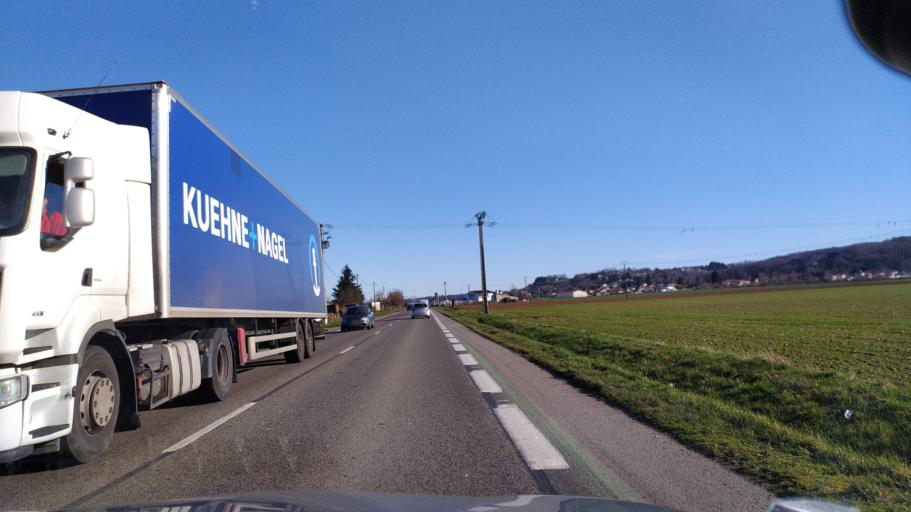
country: FR
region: Rhone-Alpes
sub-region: Departement du Rhone
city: Saint-Pierre-de-Chandieu
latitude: 45.6561
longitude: 5.0094
